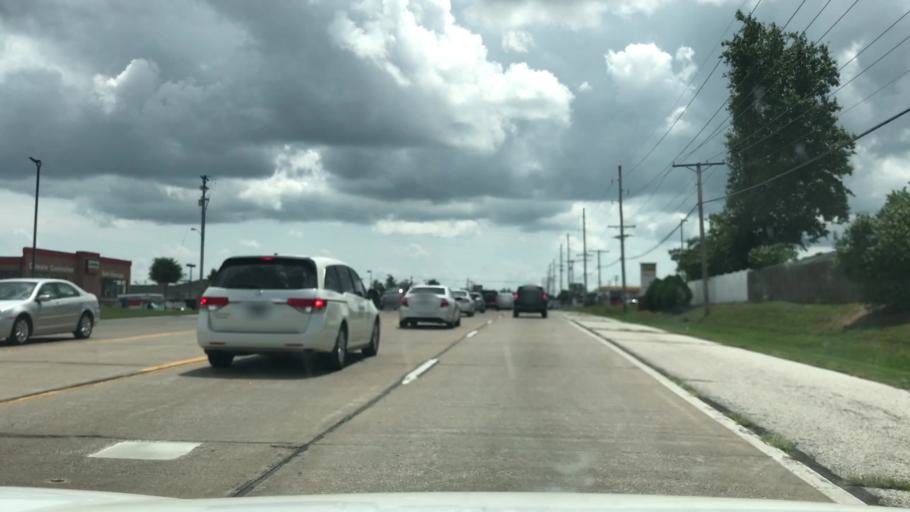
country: US
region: Missouri
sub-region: Saint Charles County
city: O'Fallon
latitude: 38.7828
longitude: -90.6999
